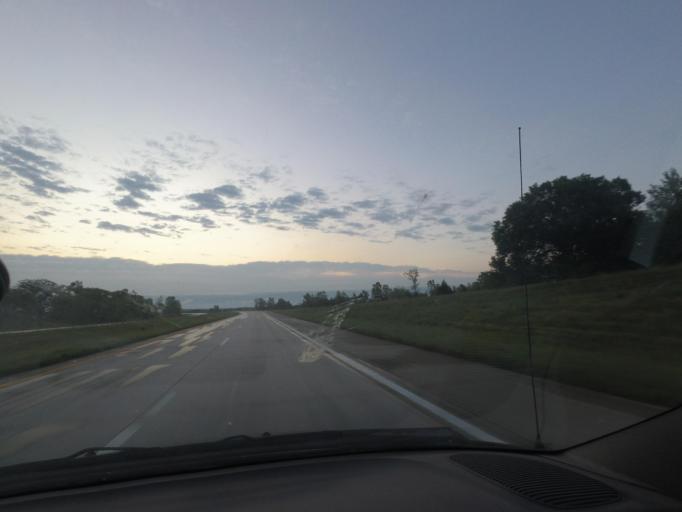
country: US
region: Missouri
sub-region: Macon County
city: Macon
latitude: 39.7543
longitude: -92.6217
